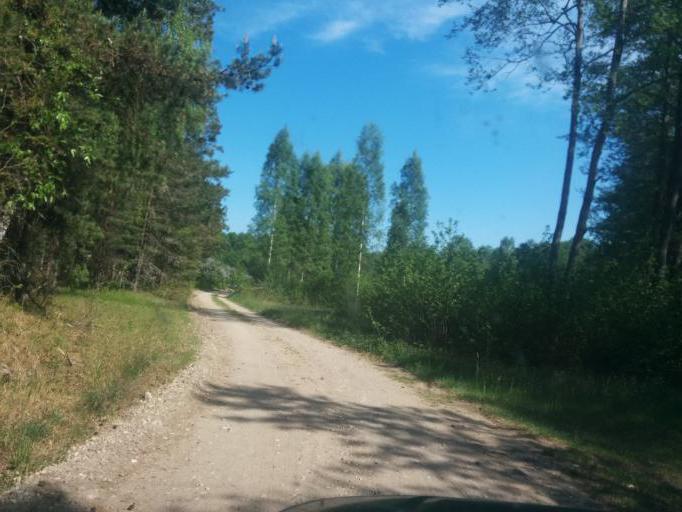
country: LV
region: Dundaga
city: Dundaga
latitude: 57.6277
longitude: 22.1127
